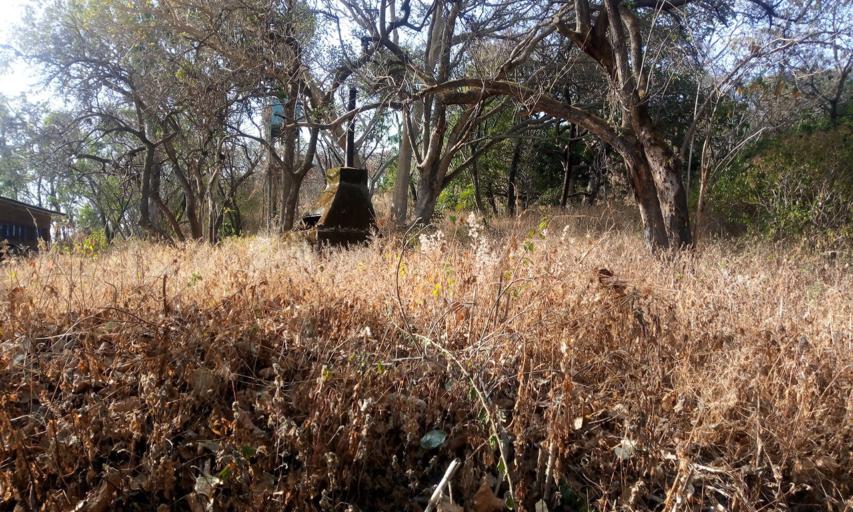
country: ET
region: Amhara
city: Gondar
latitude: 12.2383
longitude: 37.3016
